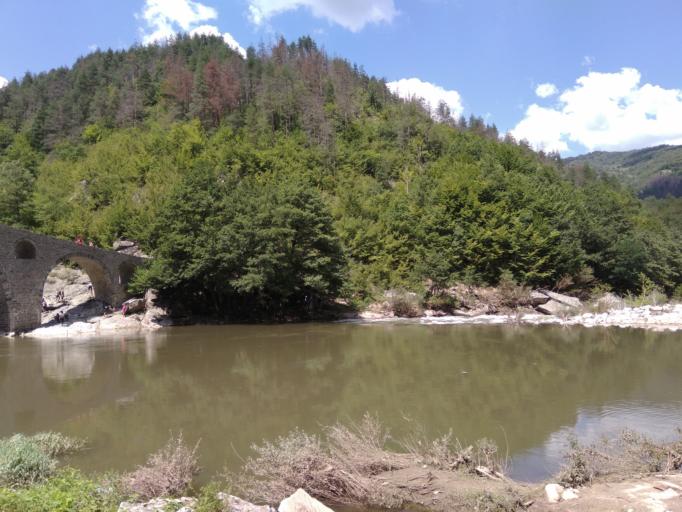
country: BG
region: Kurdzhali
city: Ardino
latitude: 41.6205
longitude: 25.1149
